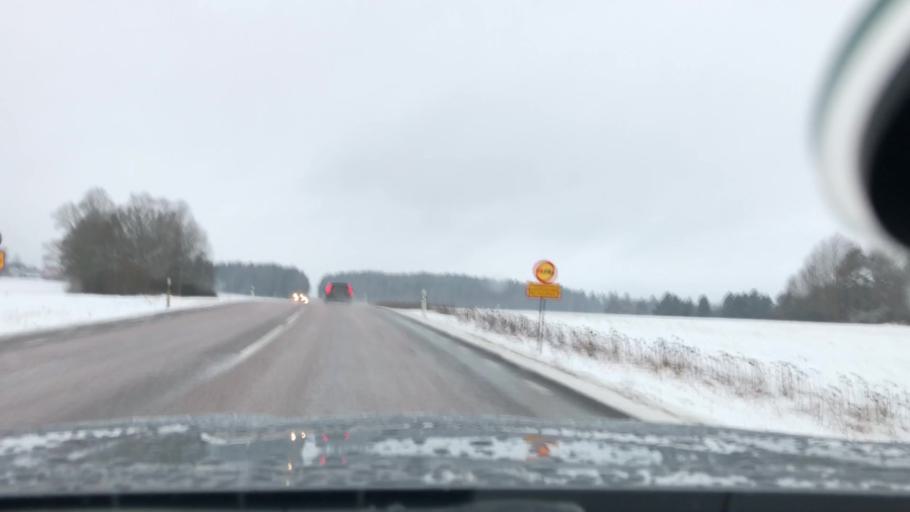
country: SE
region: Stockholm
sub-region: Sodertalje Kommun
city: Pershagen
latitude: 59.0498
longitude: 17.6078
